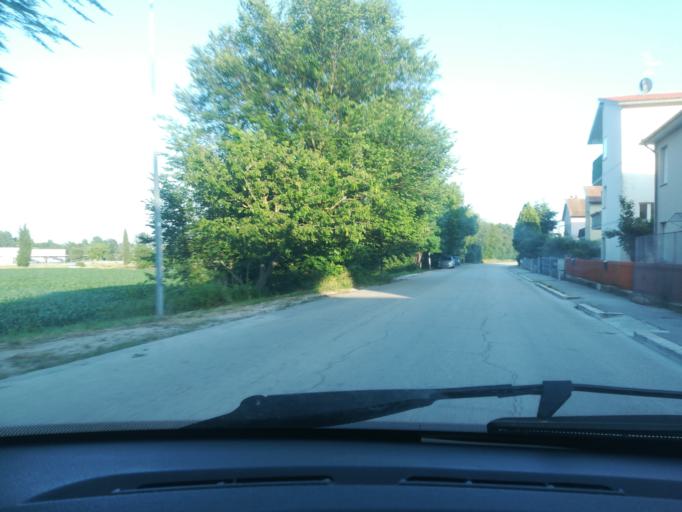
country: IT
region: The Marches
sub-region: Provincia di Macerata
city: Piediripa
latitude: 43.2800
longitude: 13.4827
